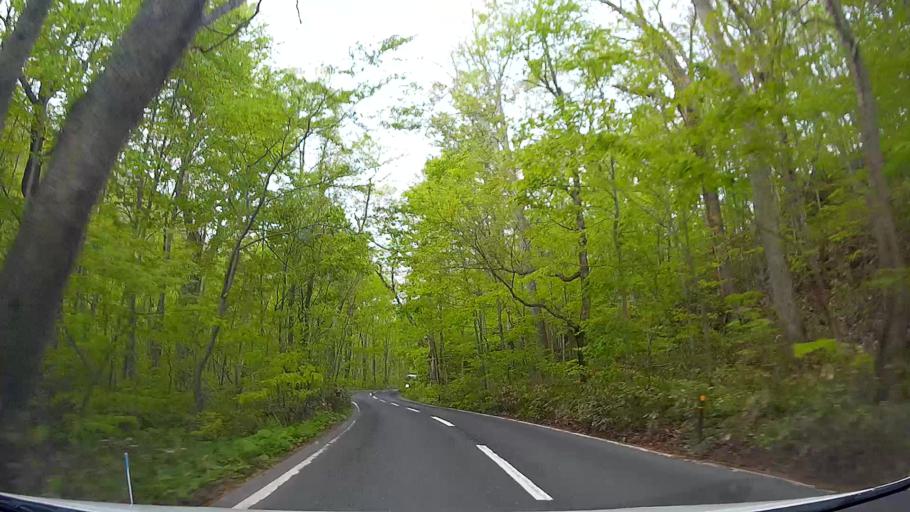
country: JP
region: Aomori
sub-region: Aomori Shi
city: Furudate
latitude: 40.5654
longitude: 140.9743
